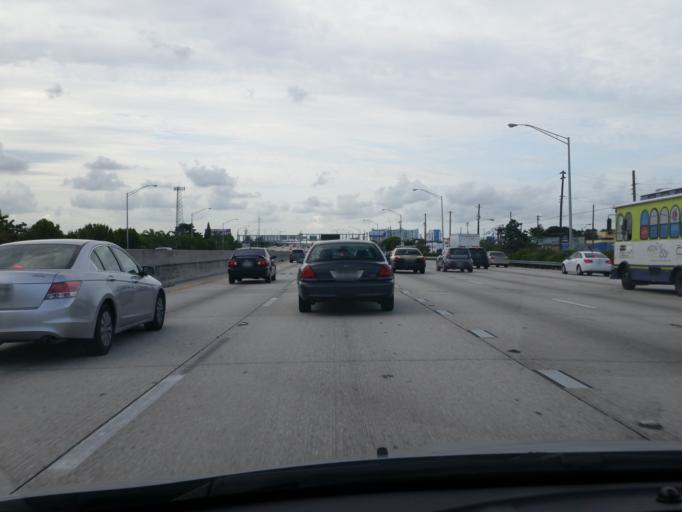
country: US
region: Florida
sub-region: Miami-Dade County
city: Allapattah
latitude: 25.7982
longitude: -80.2054
